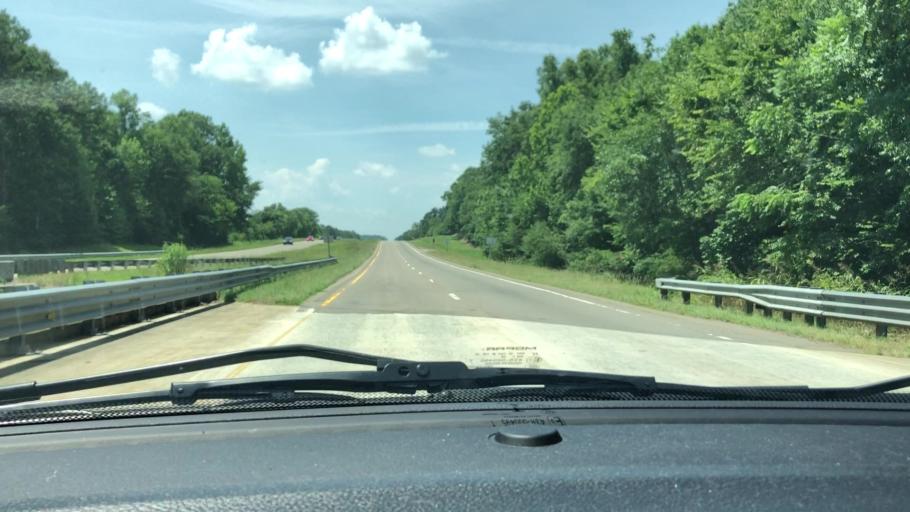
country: US
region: North Carolina
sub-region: Chatham County
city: Farmville
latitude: 35.6125
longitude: -79.3440
